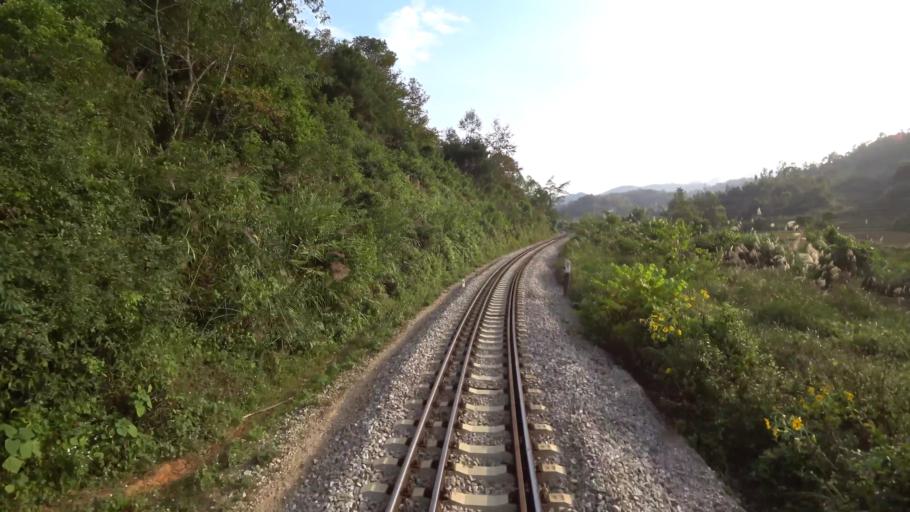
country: VN
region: Lang Son
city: Thi Tran Cao Loc
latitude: 21.9242
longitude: 106.7063
